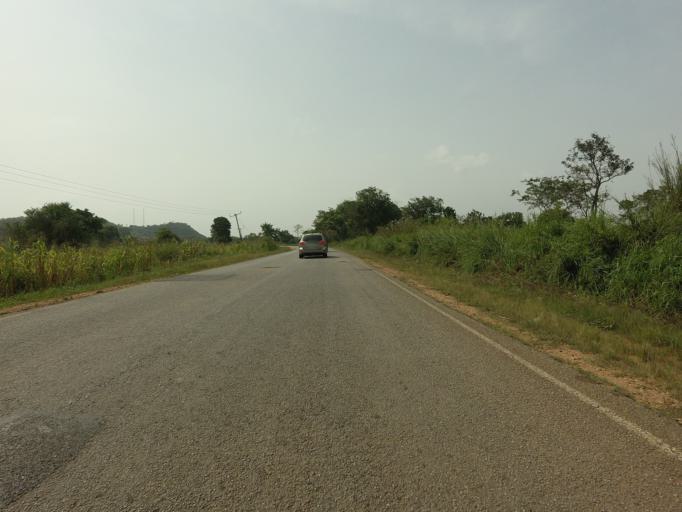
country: GH
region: Volta
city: Ho
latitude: 6.3520
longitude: 0.1753
